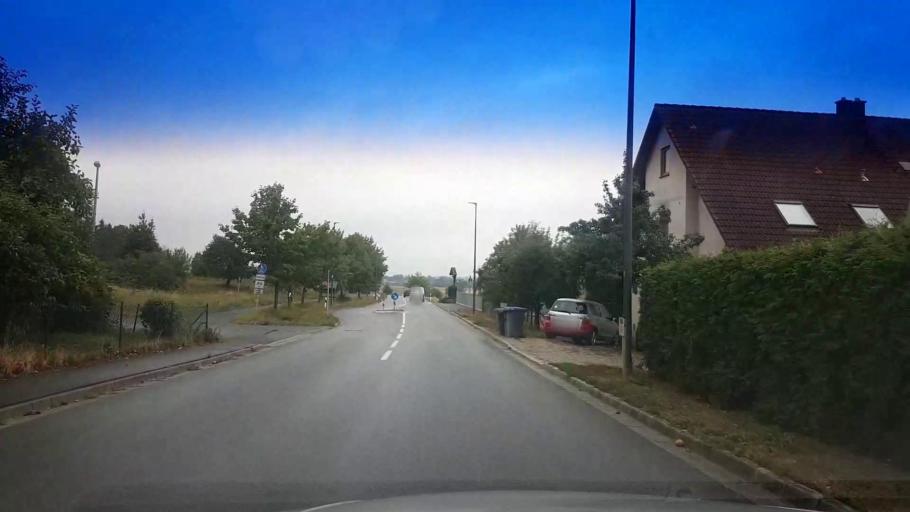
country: DE
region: Bavaria
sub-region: Upper Franconia
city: Eggolsheim
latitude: 49.7862
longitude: 11.0479
